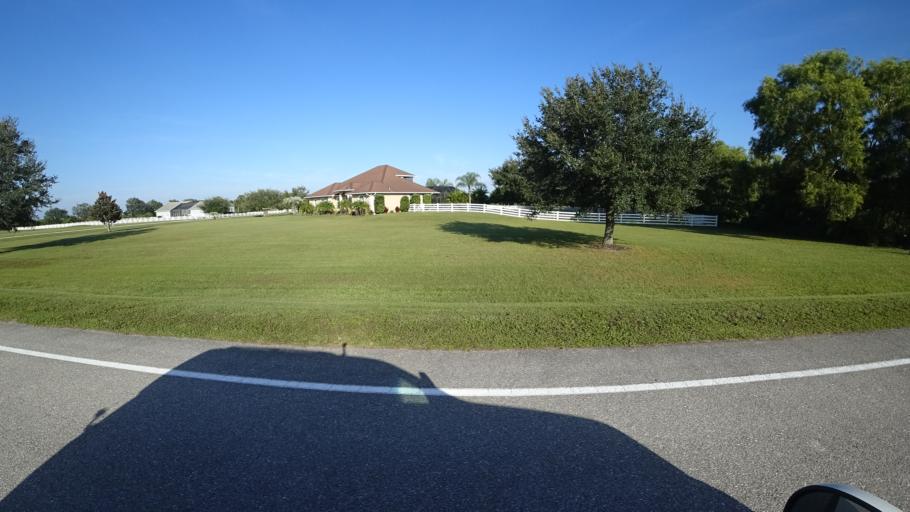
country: US
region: Florida
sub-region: Hillsborough County
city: Sun City Center
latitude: 27.5480
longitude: -82.3539
